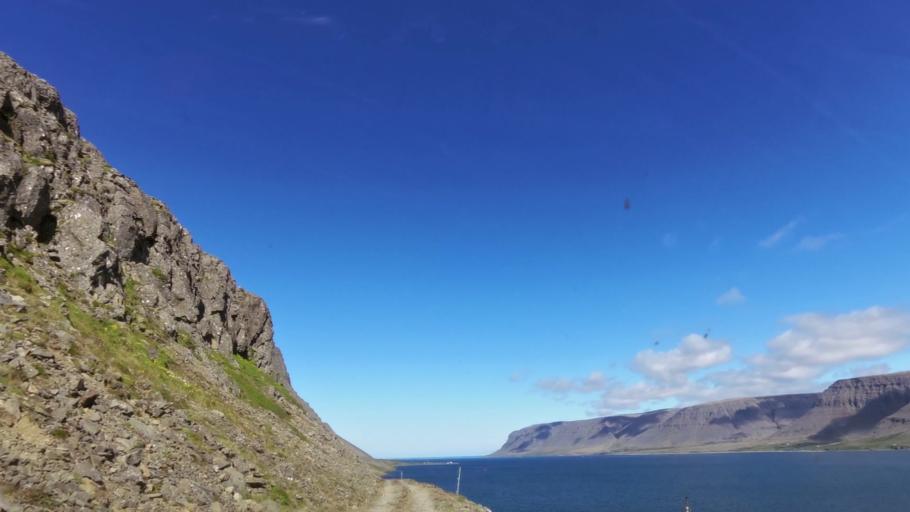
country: IS
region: West
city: Olafsvik
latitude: 65.6236
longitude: -23.8860
